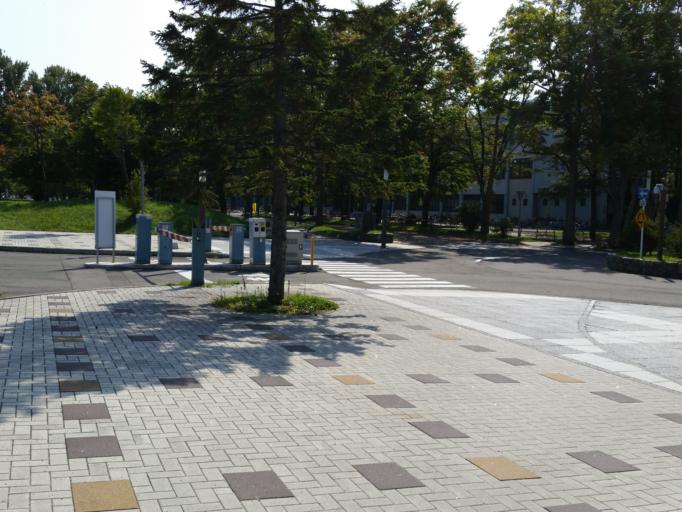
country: JP
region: Hokkaido
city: Sapporo
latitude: 43.0810
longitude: 141.3408
